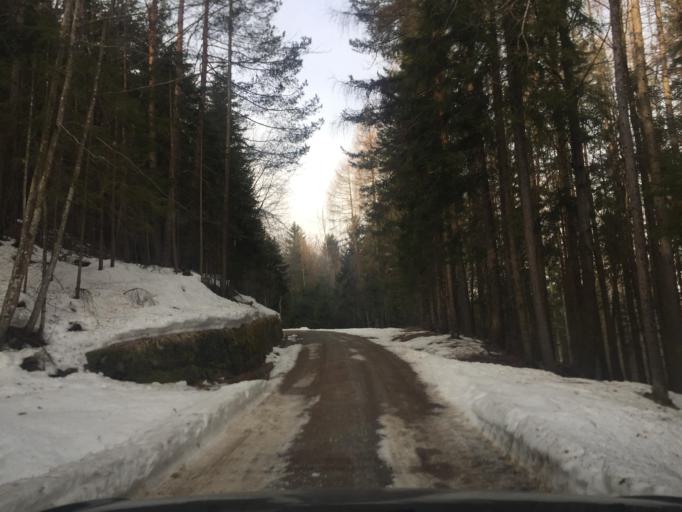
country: AT
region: Carinthia
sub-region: Politischer Bezirk Villach Land
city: Hohenthurn
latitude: 46.5107
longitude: 13.6542
